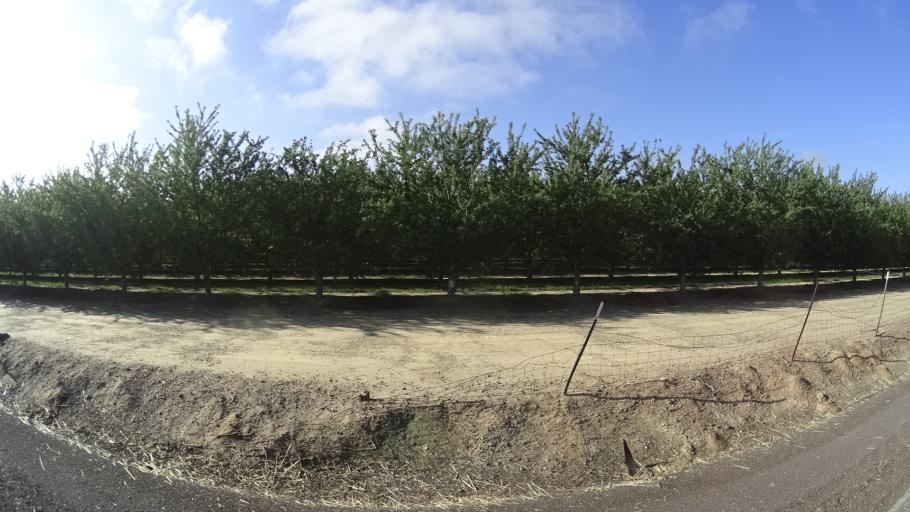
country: US
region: California
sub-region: Glenn County
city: Willows
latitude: 39.5822
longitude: -122.1389
